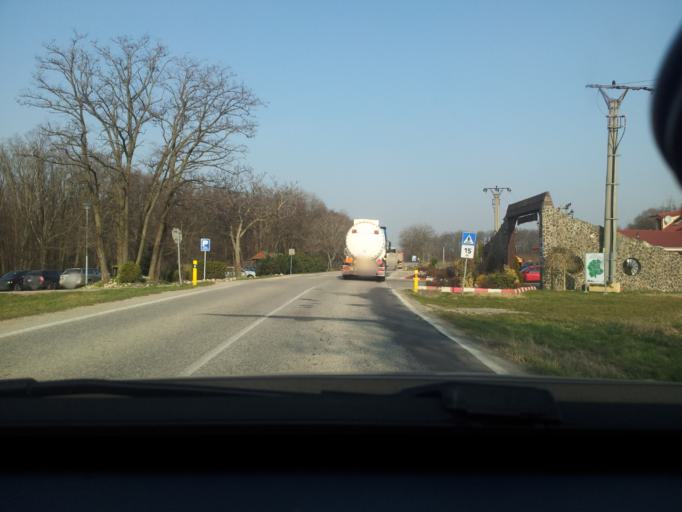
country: SK
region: Nitriansky
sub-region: Okres Nitra
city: Nitra
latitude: 48.3326
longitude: 18.0062
